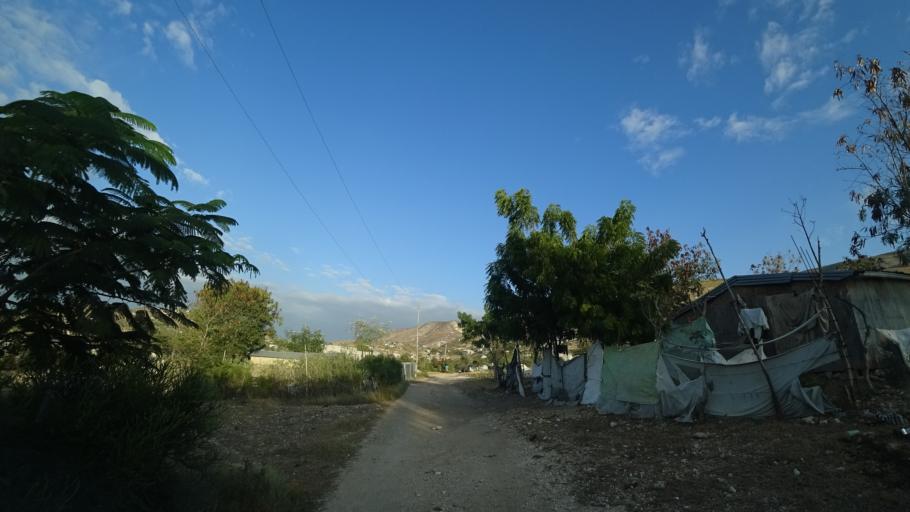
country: HT
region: Ouest
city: Croix des Bouquets
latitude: 18.6706
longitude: -72.2817
